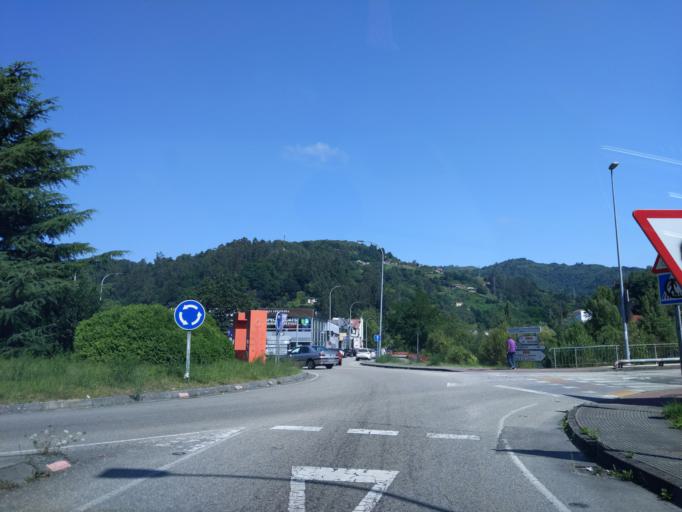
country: ES
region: Asturias
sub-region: Province of Asturias
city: El entrego
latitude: 43.2846
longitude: -5.6250
